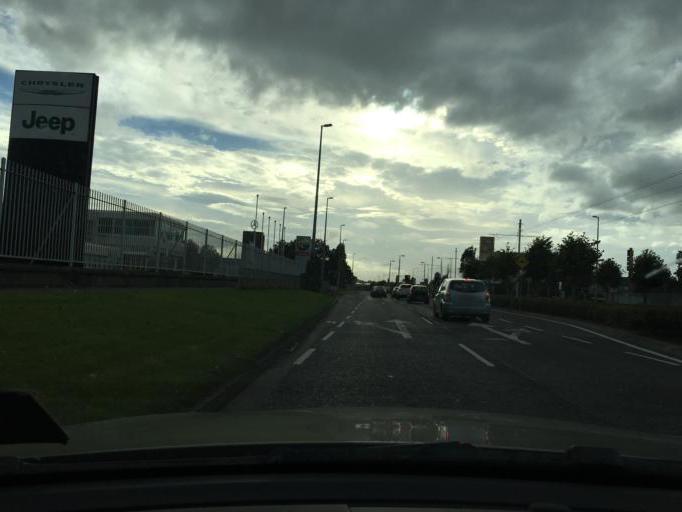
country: IE
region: Leinster
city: Crumlin
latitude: 53.3271
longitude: -6.3410
